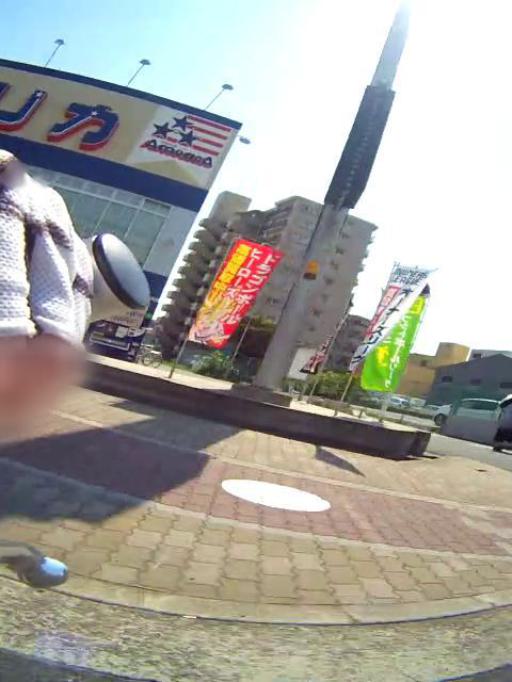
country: JP
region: Osaka
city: Yao
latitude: 34.6384
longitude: 135.5511
